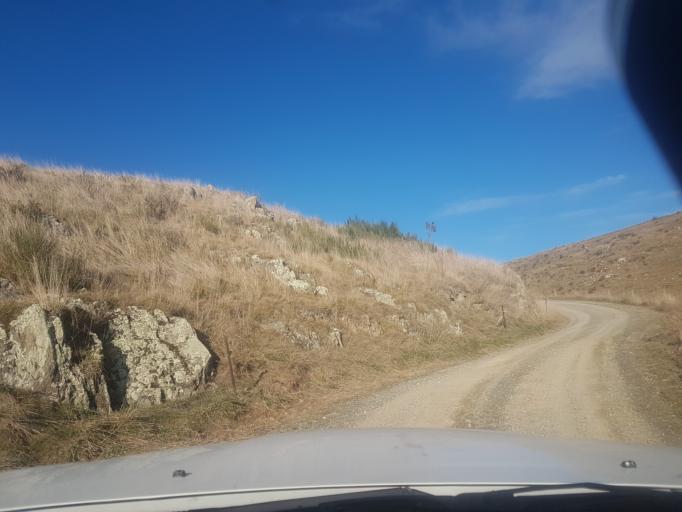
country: NZ
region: Canterbury
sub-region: Timaru District
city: Pleasant Point
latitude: -44.1758
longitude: 170.8882
